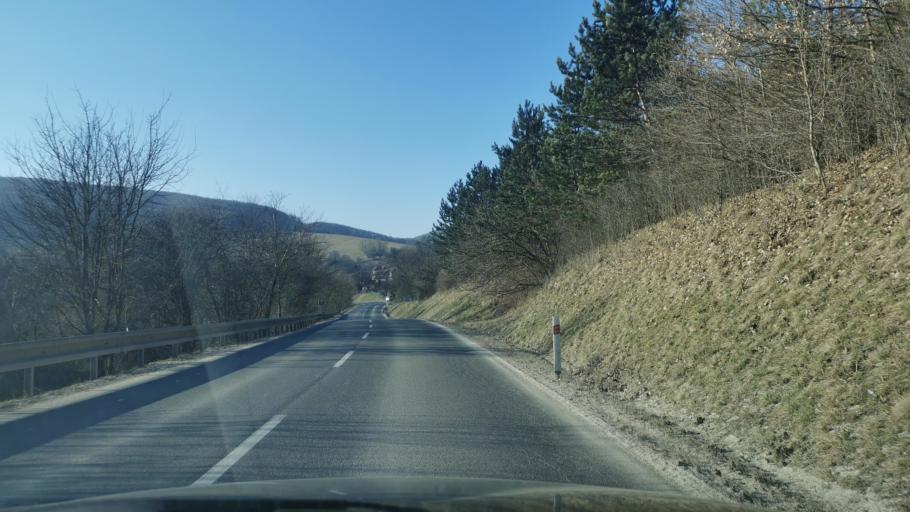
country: SK
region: Trenciansky
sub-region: Okres Myjava
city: Myjava
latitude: 48.7510
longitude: 17.5027
